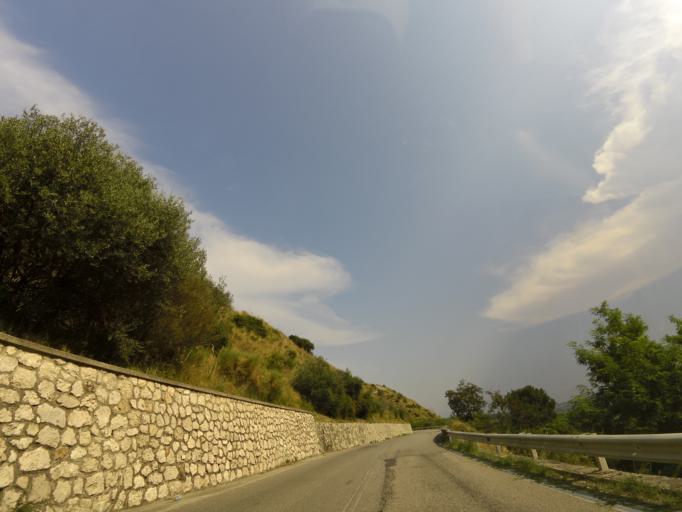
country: IT
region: Calabria
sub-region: Provincia di Reggio Calabria
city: Monasterace
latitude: 38.4597
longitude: 16.5217
